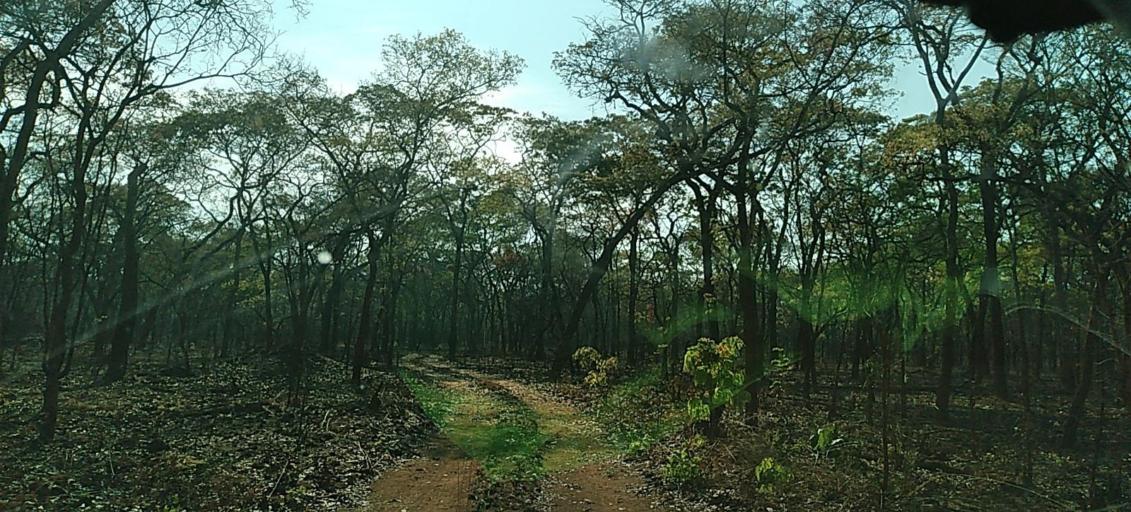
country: ZM
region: North-Western
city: Kalengwa
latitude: -13.2265
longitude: 25.0931
